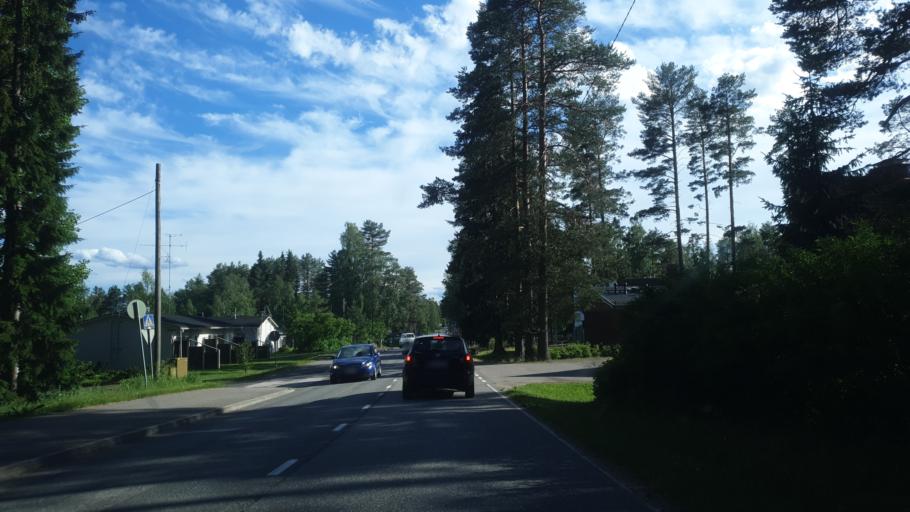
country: FI
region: Southern Savonia
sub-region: Mikkeli
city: Pertunmaa
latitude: 61.5084
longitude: 26.4827
